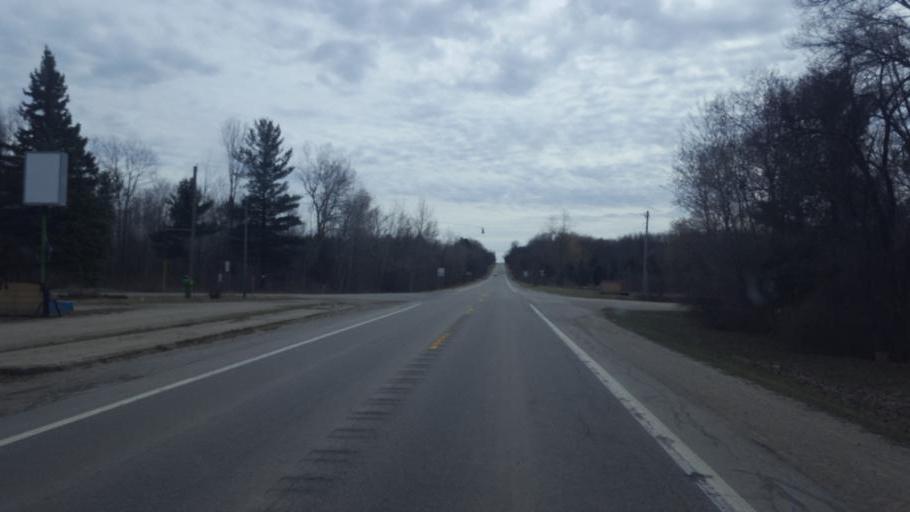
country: US
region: Michigan
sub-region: Isabella County
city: Lake Isabella
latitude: 43.6907
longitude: -85.1466
